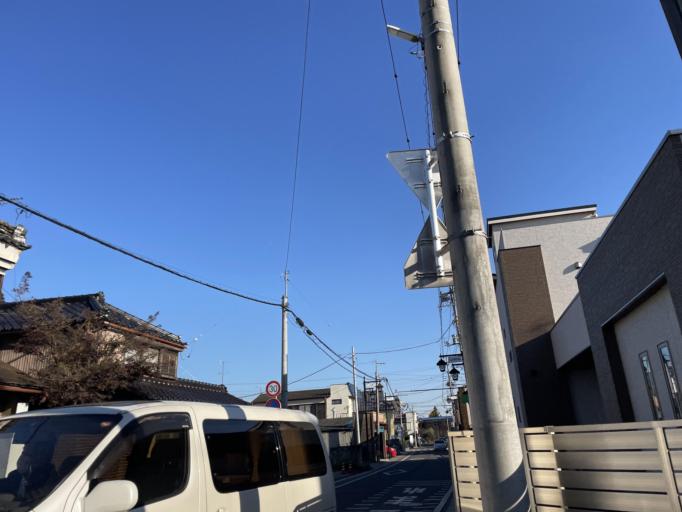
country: JP
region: Ibaraki
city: Sakai
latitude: 36.1054
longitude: 139.7907
